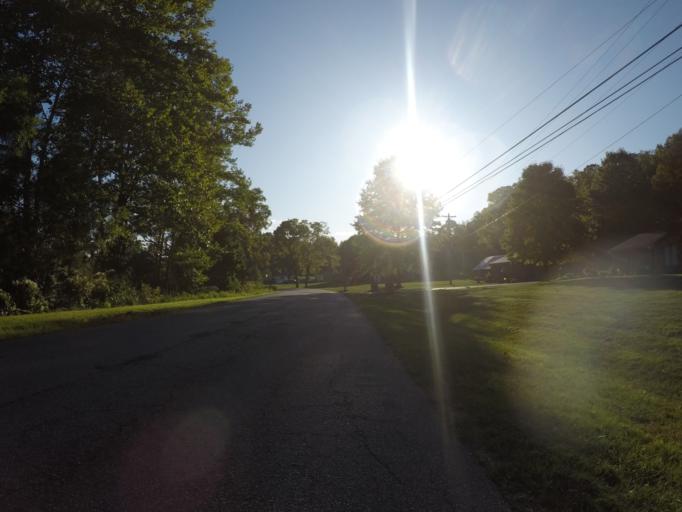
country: US
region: Ohio
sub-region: Lawrence County
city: Coal Grove
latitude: 38.5388
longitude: -82.5389
